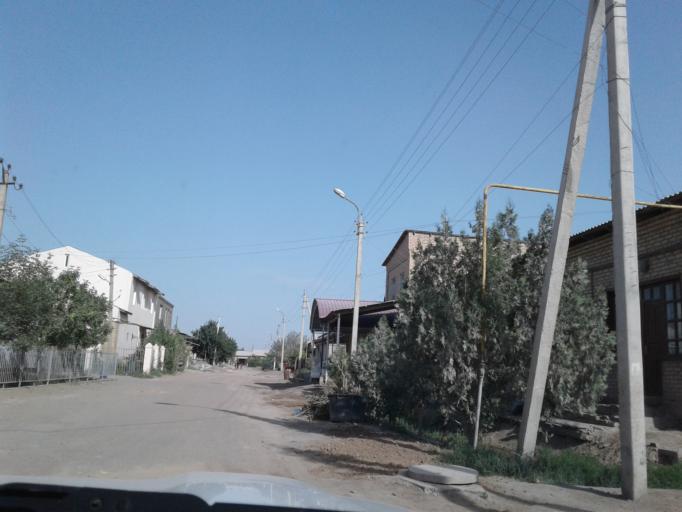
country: TM
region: Dasoguz
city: Dasoguz
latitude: 41.8486
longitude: 59.9243
